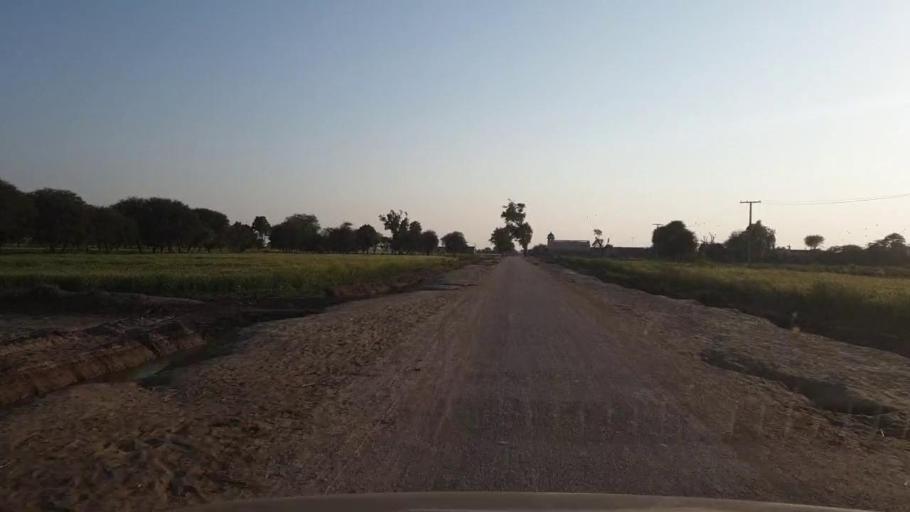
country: PK
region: Sindh
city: Digri
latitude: 25.0991
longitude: 69.2851
